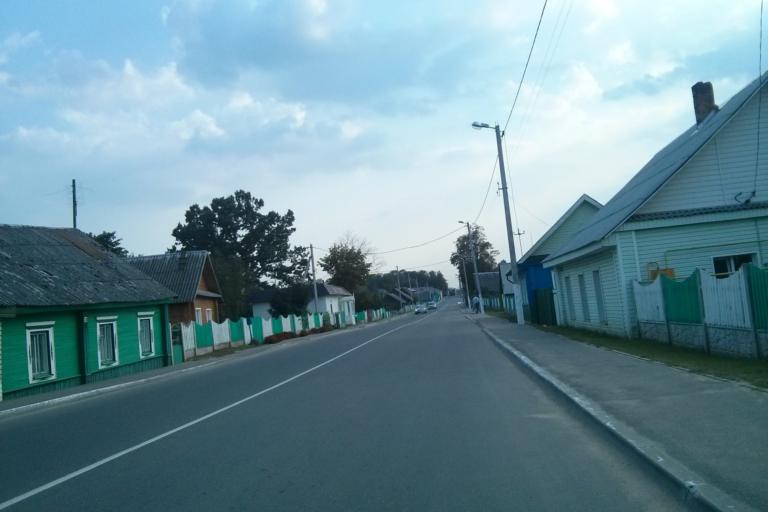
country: BY
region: Minsk
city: Chervyen'
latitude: 53.7187
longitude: 28.4182
